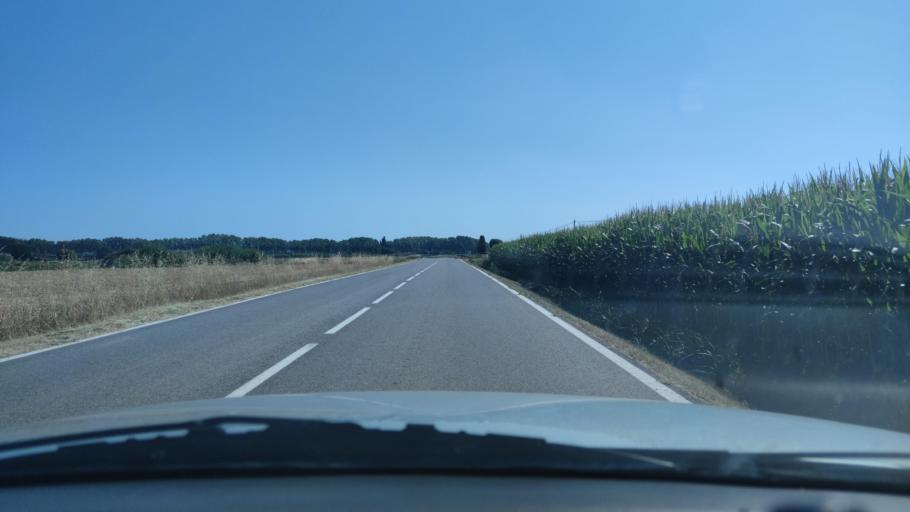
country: ES
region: Catalonia
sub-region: Provincia de Lleida
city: Linyola
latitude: 41.7227
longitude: 0.9188
